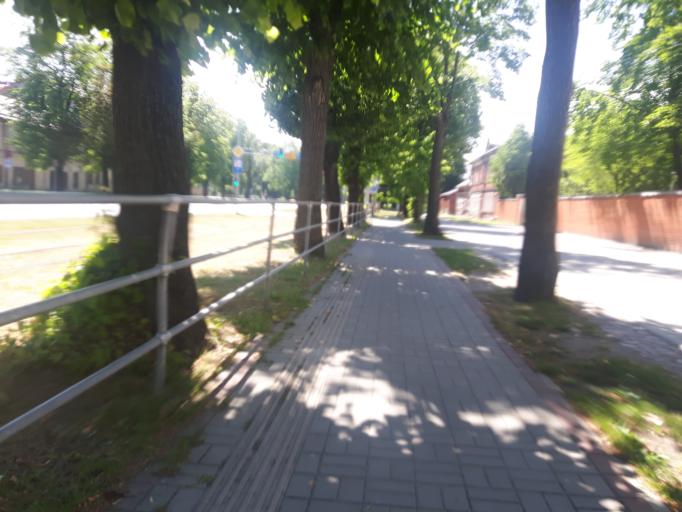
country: LV
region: Liepaja
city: Liepaja
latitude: 56.5237
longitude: 21.0259
